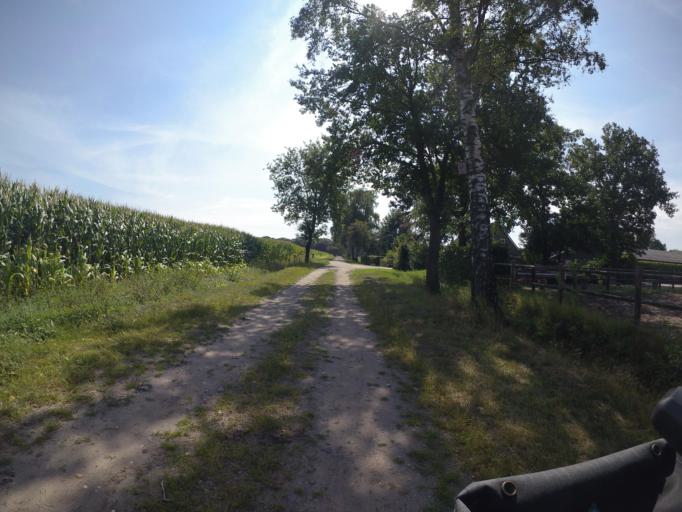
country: NL
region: North Brabant
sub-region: Bergeijk
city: Bergeyk
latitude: 51.3632
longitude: 5.3639
